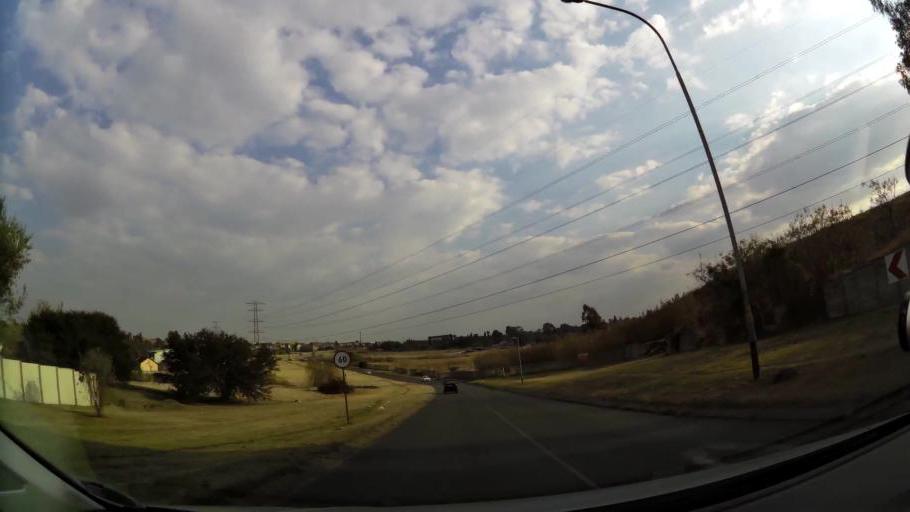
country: ZA
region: Gauteng
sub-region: City of Johannesburg Metropolitan Municipality
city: Modderfontein
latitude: -26.1301
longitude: 28.1849
